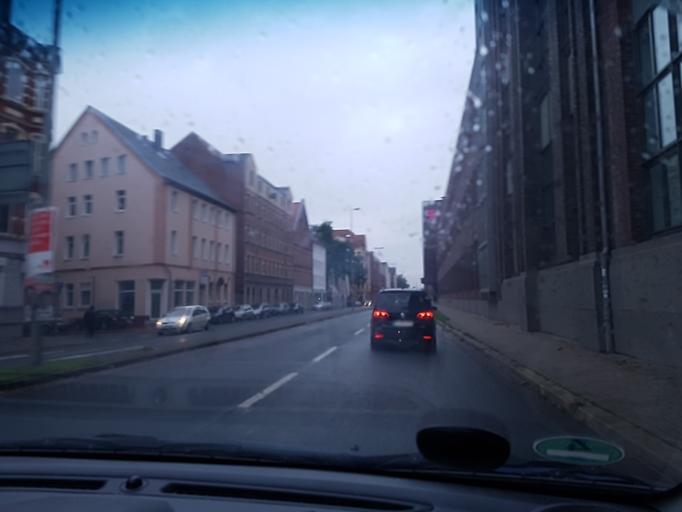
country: DE
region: Lower Saxony
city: Hannover
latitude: 52.3607
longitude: 9.7152
